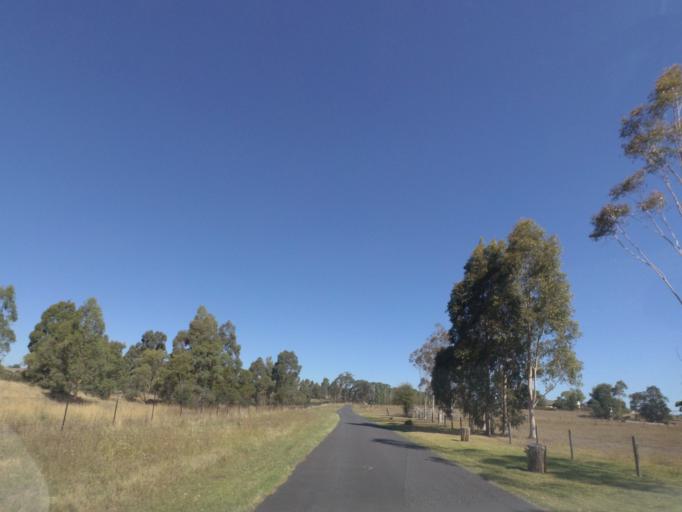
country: AU
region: Victoria
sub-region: Yarra Ranges
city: Chirnside Park
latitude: -37.7200
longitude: 145.2928
